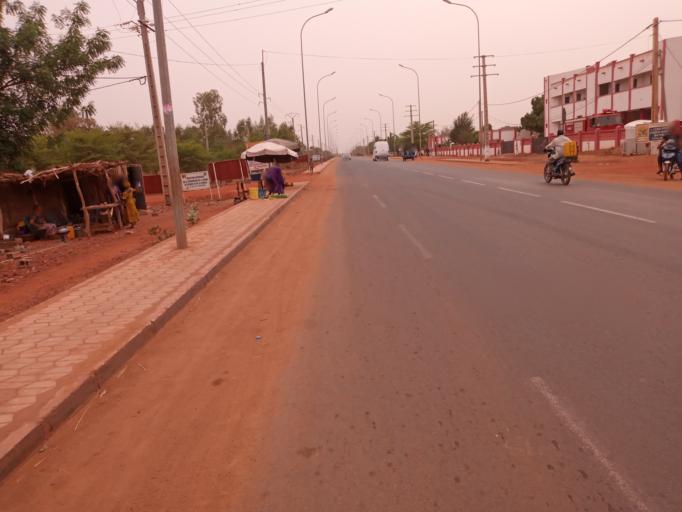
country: ML
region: Koulikoro
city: Koulikoro
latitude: 12.8428
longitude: -7.5860
